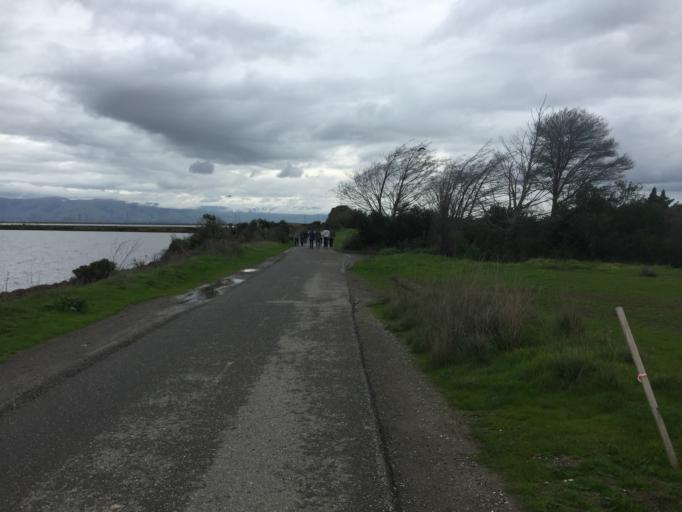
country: US
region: California
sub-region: Santa Clara County
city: Mountain View
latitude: 37.4353
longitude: -122.0895
